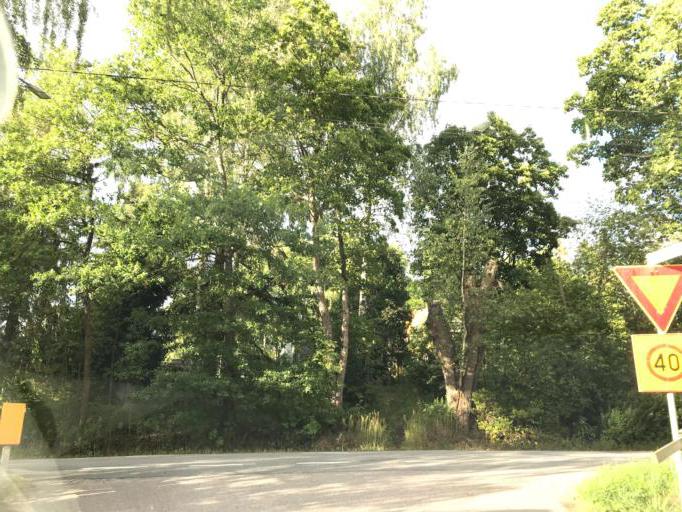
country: FI
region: Uusimaa
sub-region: Helsinki
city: Vihti
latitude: 60.4007
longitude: 24.4940
